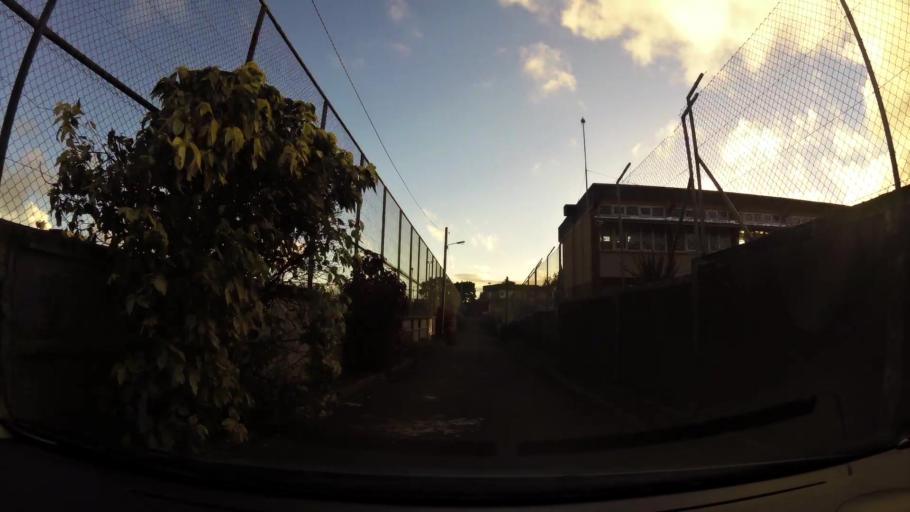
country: MU
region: Plaines Wilhems
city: Curepipe
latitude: -20.3060
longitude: 57.5325
